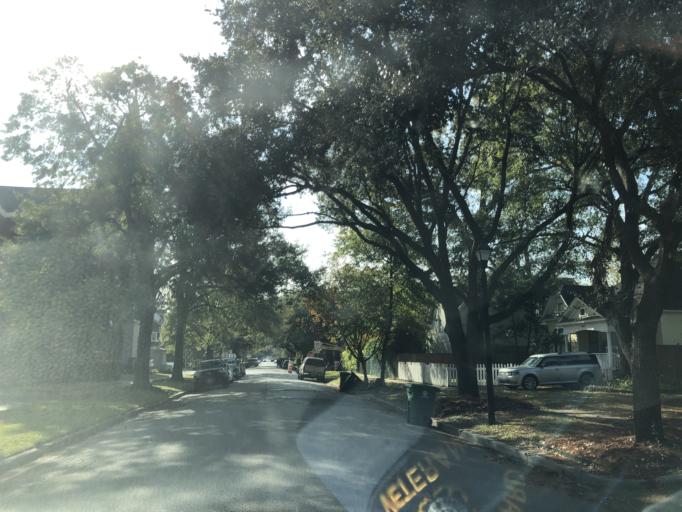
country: US
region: Texas
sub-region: Harris County
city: Houston
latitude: 29.7897
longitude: -95.3964
